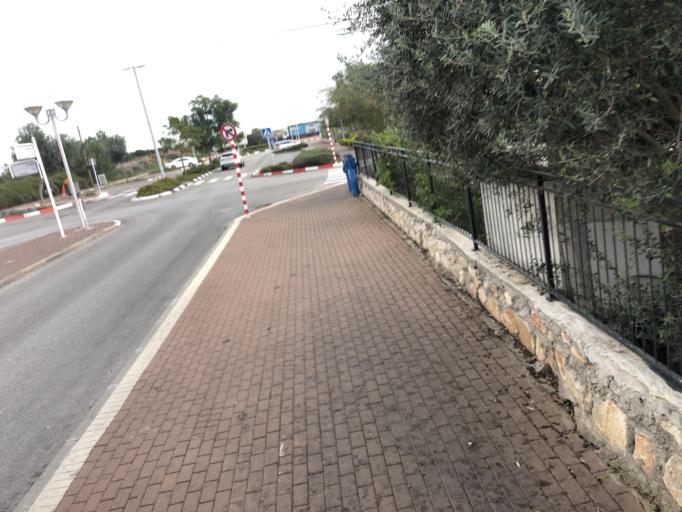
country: IL
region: Northern District
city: `Akko
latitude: 32.9327
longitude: 35.0950
